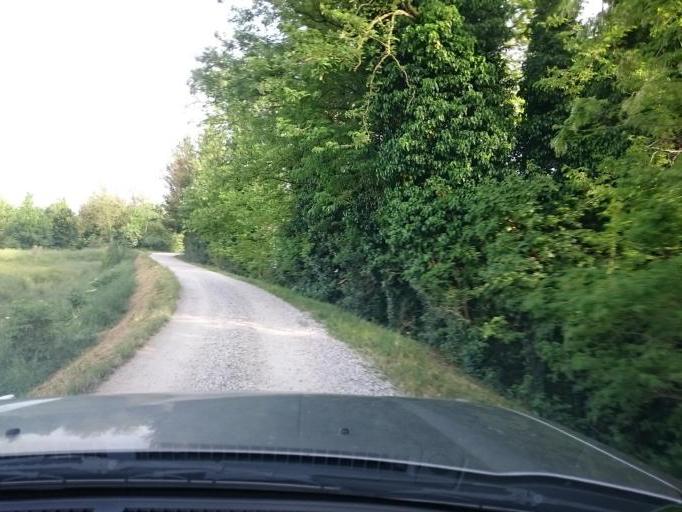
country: IT
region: Veneto
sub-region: Provincia di Padova
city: Ponte San Nicolo
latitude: 45.3879
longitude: 11.9174
